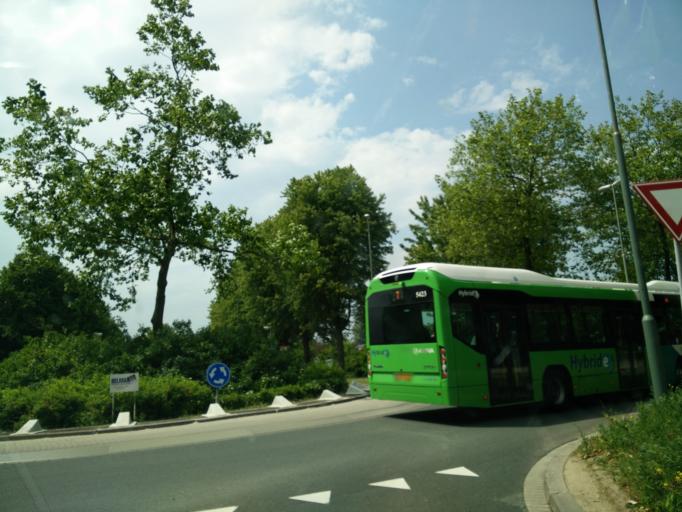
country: NL
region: South Holland
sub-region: Gemeente Dordrecht
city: Dordrecht
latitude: 51.7841
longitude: 4.6723
